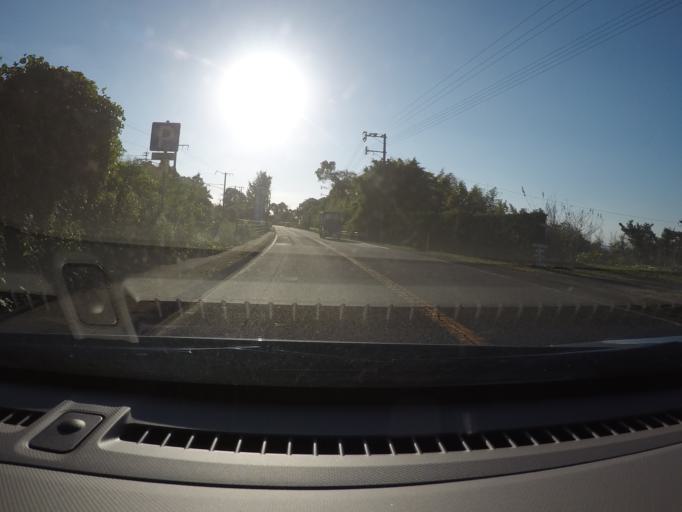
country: JP
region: Kagoshima
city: Izumi
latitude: 32.1490
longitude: 130.3614
